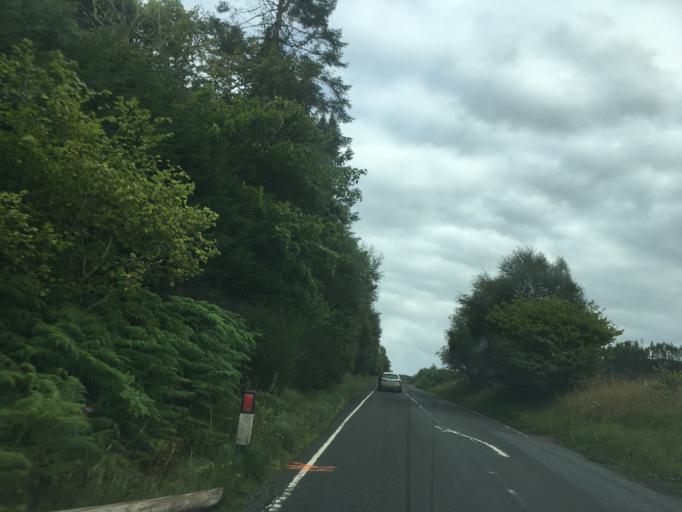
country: GB
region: Scotland
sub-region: Argyll and Bute
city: Oban
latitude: 56.3200
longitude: -5.4934
